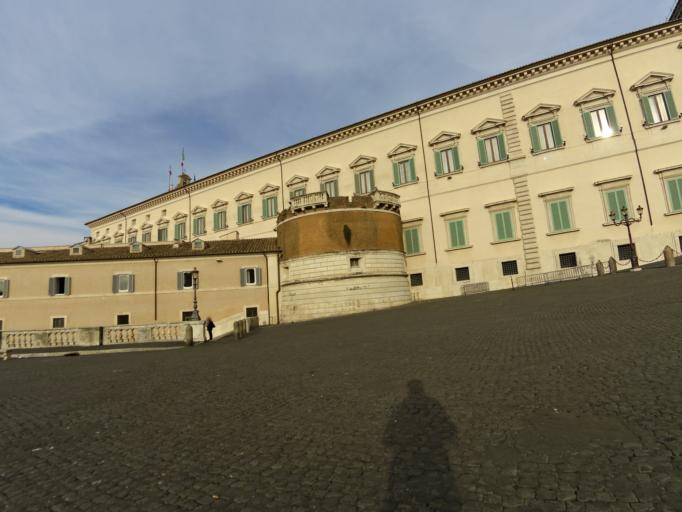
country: IT
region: Latium
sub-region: Citta metropolitana di Roma Capitale
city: Rome
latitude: 41.8995
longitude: 12.4863
